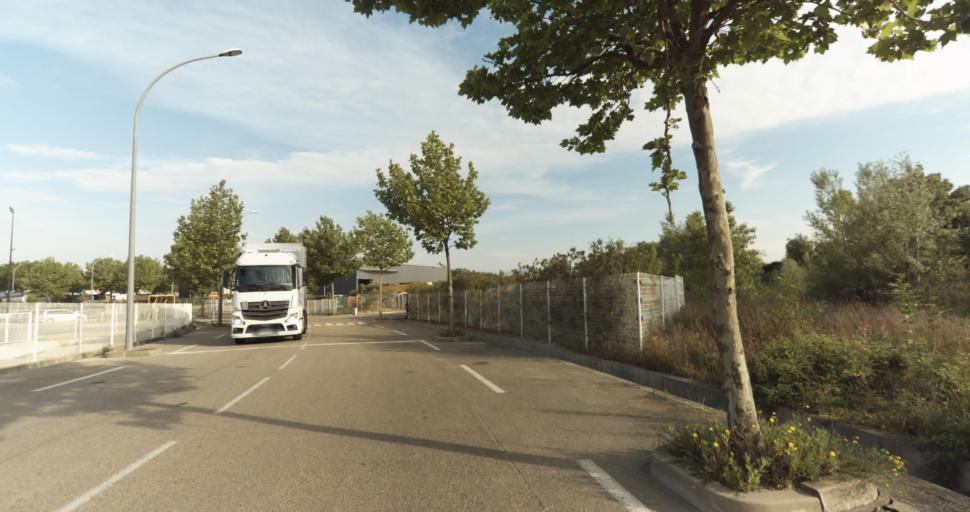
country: FR
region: Languedoc-Roussillon
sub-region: Departement du Gard
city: Rodilhan
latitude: 43.8395
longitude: 4.4287
